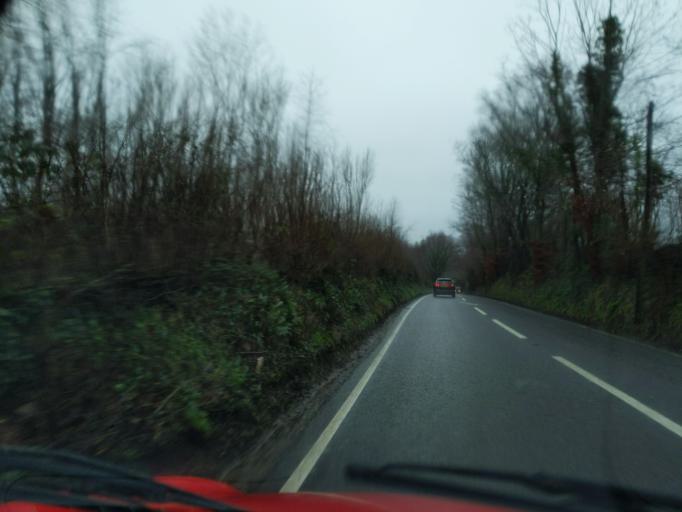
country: GB
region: England
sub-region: Cornwall
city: South Hill
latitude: 50.5780
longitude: -4.3335
